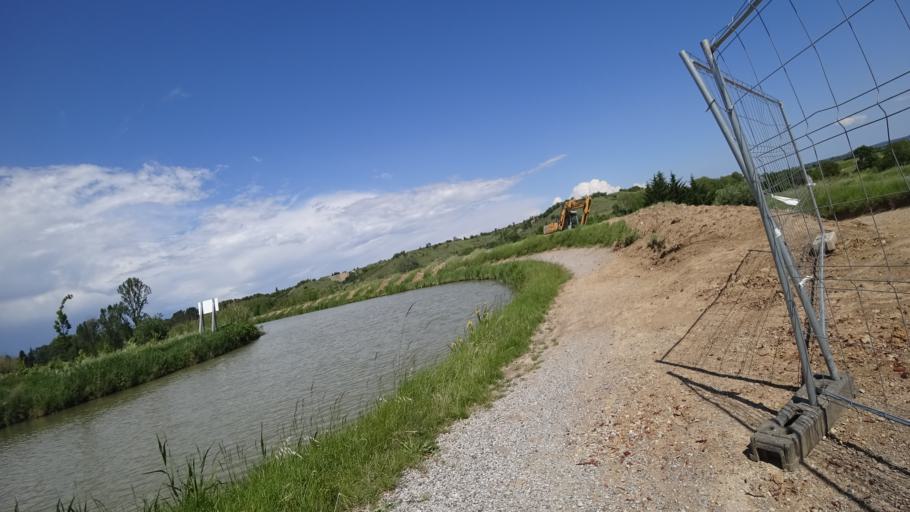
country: FR
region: Languedoc-Roussillon
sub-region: Departement de l'Aude
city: Canet
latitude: 43.2486
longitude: 2.8393
